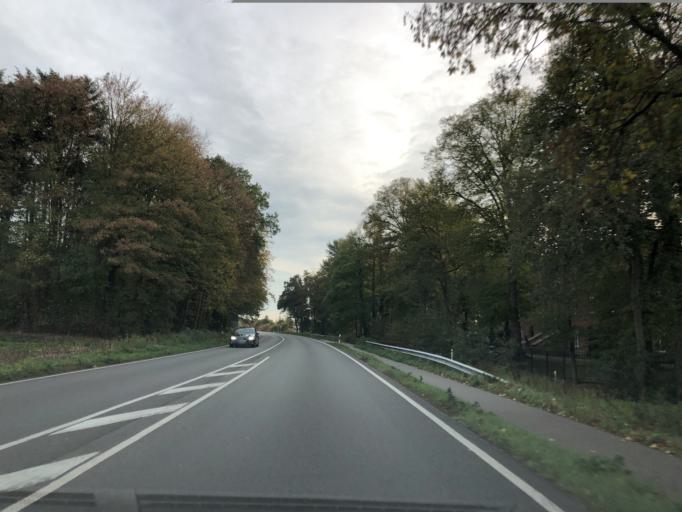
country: DE
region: Lower Saxony
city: Lehe
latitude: 53.0376
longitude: 7.3252
